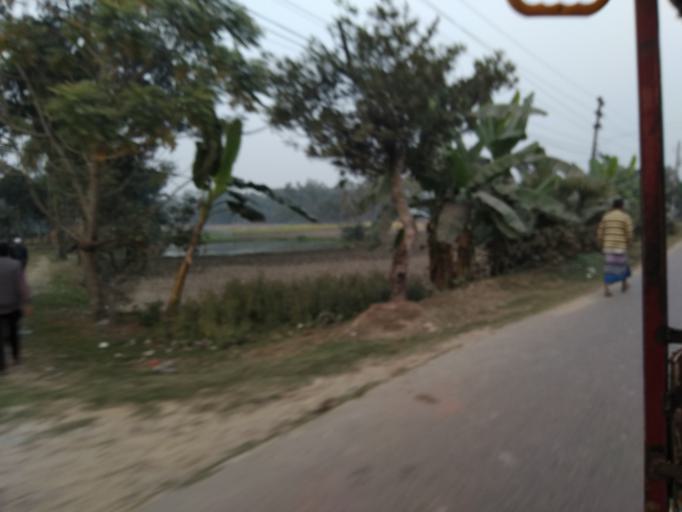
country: BD
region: Dhaka
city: Netrakona
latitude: 24.8679
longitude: 90.7048
